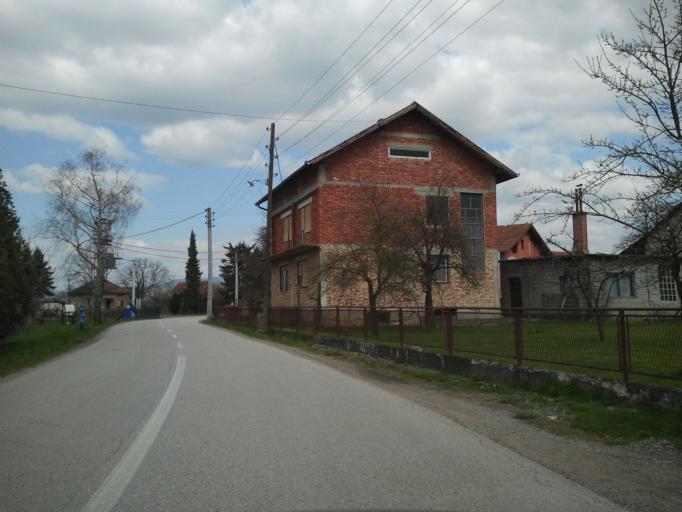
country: HR
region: Grad Zagreb
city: Zadvorsko
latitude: 45.7430
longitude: 15.9582
